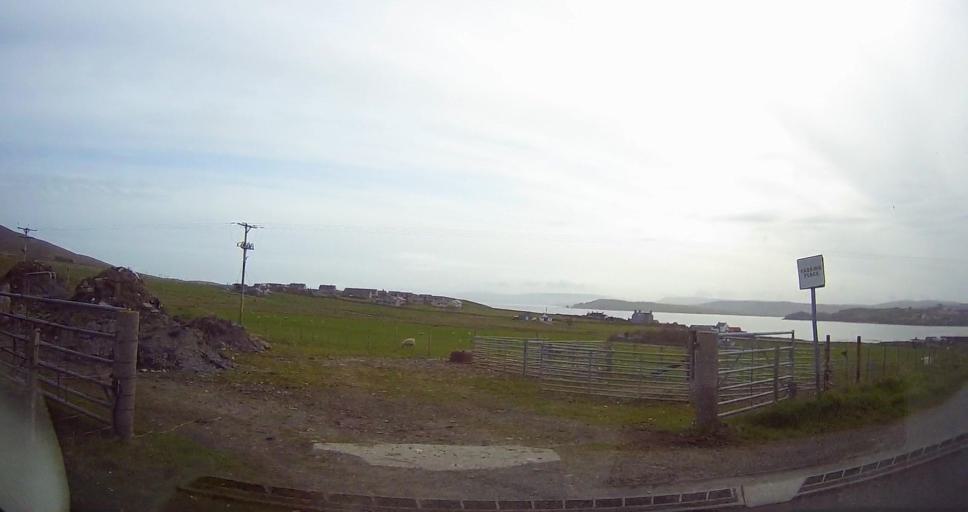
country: GB
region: Scotland
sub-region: Shetland Islands
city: Shetland
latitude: 60.1500
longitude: -1.1068
